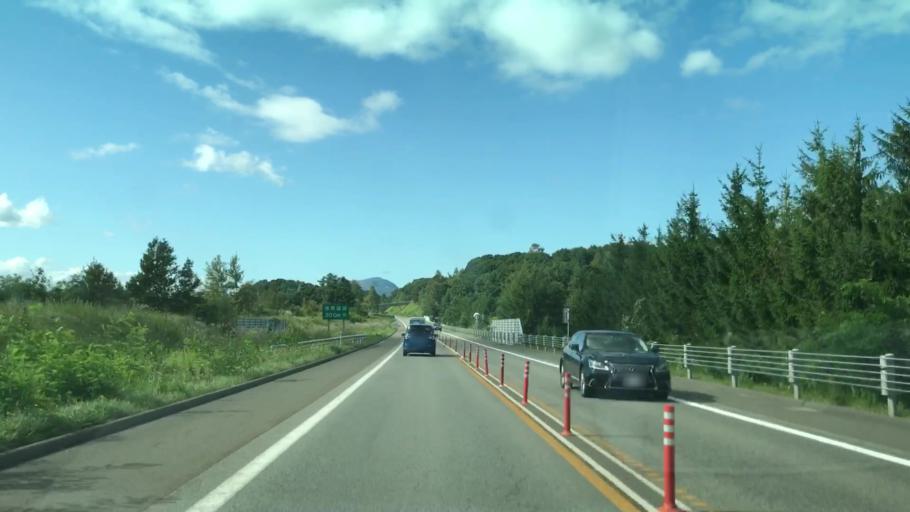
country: JP
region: Hokkaido
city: Date
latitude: 42.4333
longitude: 140.9234
